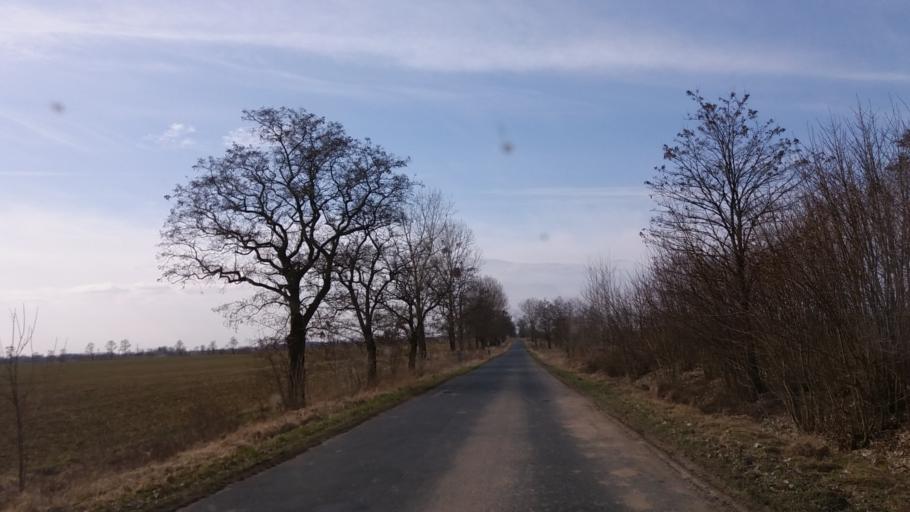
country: PL
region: West Pomeranian Voivodeship
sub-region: Powiat choszczenski
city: Krzecin
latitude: 53.1584
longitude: 15.5085
